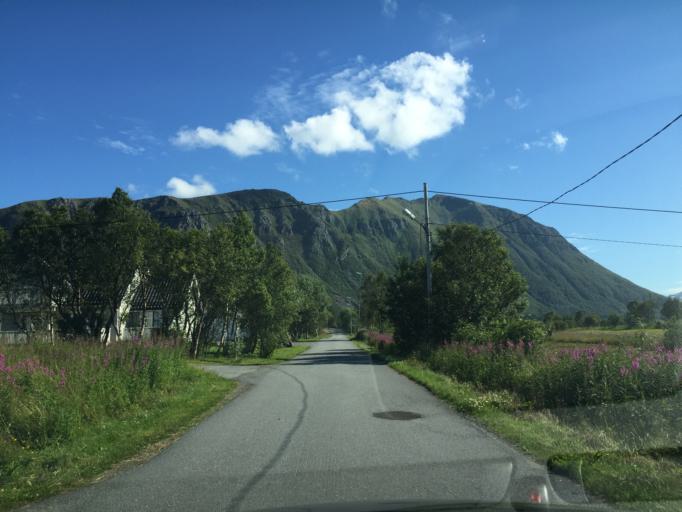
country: NO
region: Nordland
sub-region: Vagan
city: Kabelvag
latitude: 68.3920
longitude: 14.4672
